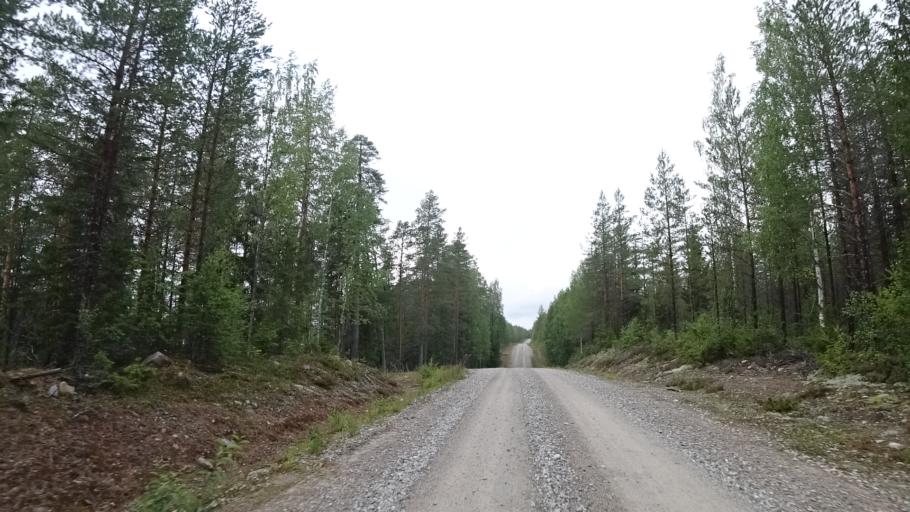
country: FI
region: North Karelia
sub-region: Pielisen Karjala
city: Lieksa
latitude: 63.4665
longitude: 30.2910
